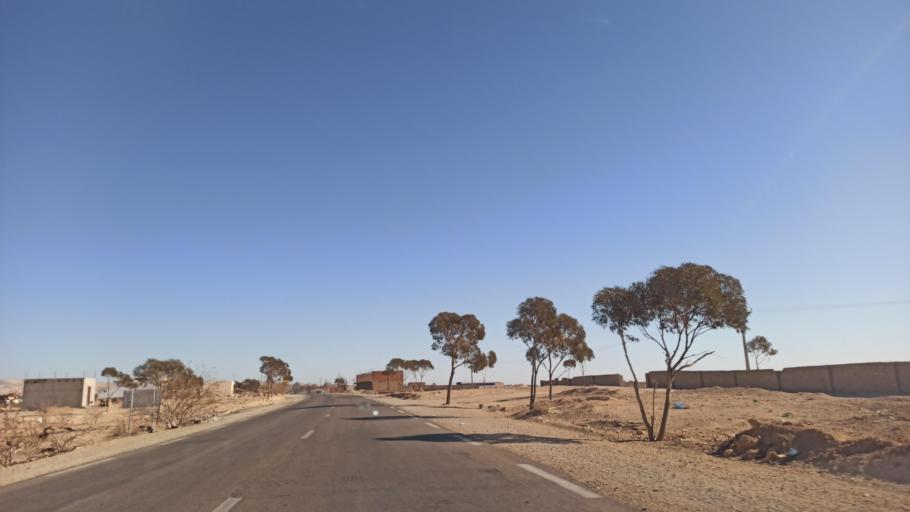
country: TN
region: Gafsa
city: Al Metlaoui
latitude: 34.3078
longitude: 8.3726
